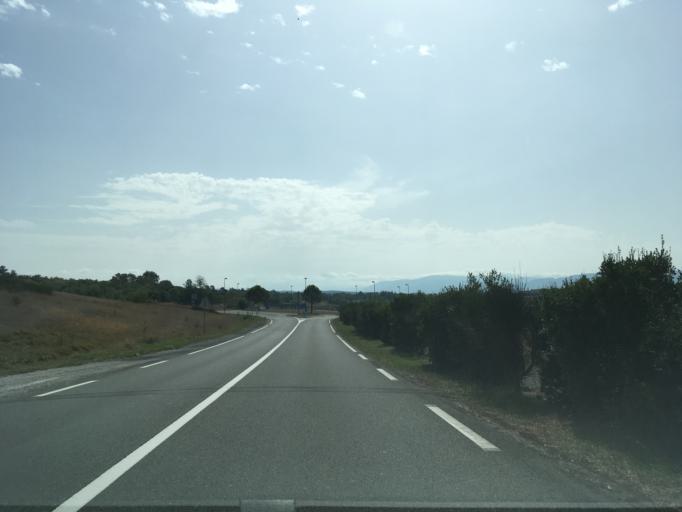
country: FR
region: Midi-Pyrenees
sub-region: Departement du Tarn
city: Lagarrigue
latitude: 43.5694
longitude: 2.2579
